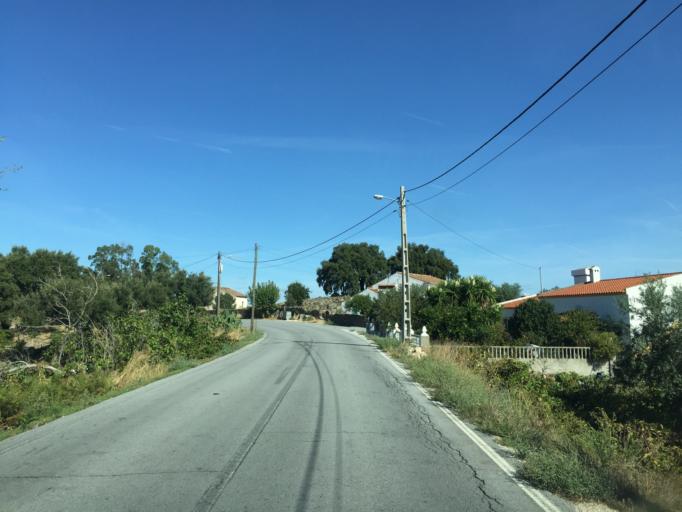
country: PT
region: Portalegre
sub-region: Marvao
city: Marvao
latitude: 39.4387
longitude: -7.3652
